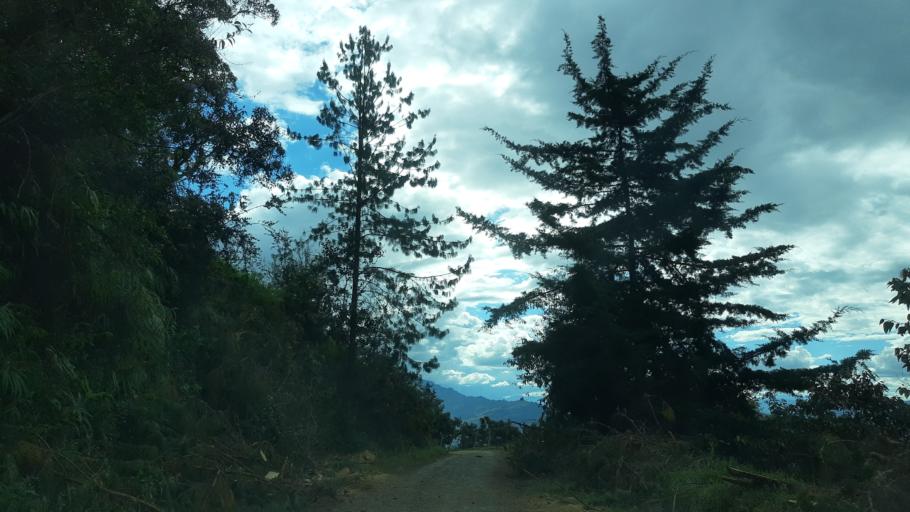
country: CO
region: Boyaca
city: Garagoa
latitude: 5.0089
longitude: -73.3408
